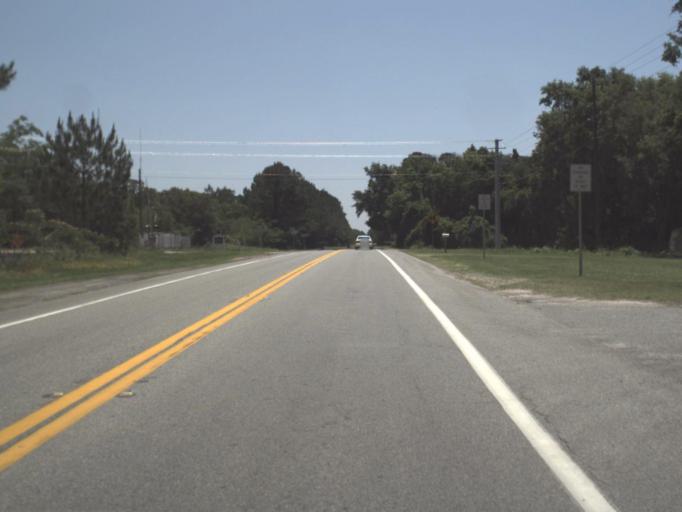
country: US
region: Florida
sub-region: Suwannee County
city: Live Oak
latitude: 30.3620
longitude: -83.1312
